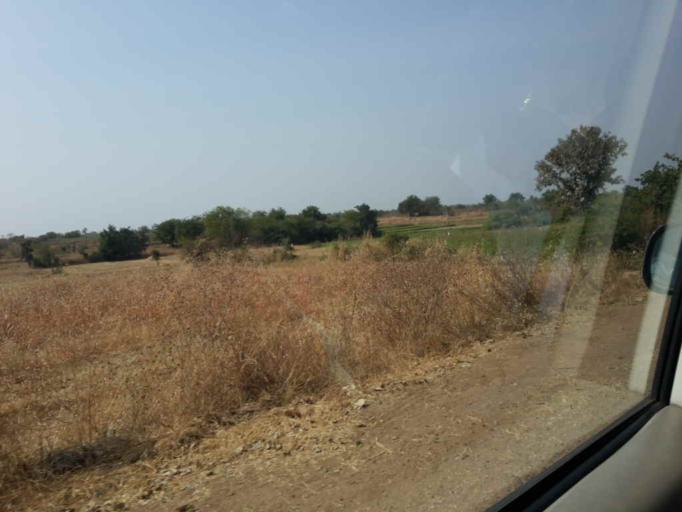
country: IN
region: Telangana
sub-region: Karimnagar
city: Sirsilla
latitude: 18.2771
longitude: 78.8524
